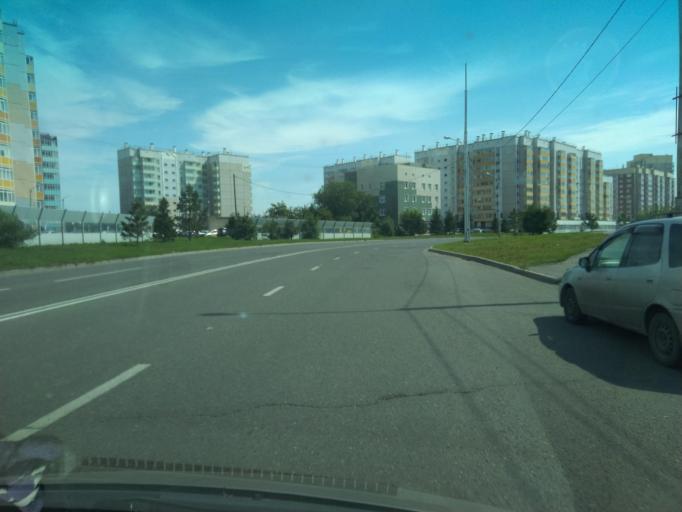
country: RU
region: Krasnoyarskiy
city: Solnechnyy
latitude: 56.0536
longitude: 92.9214
